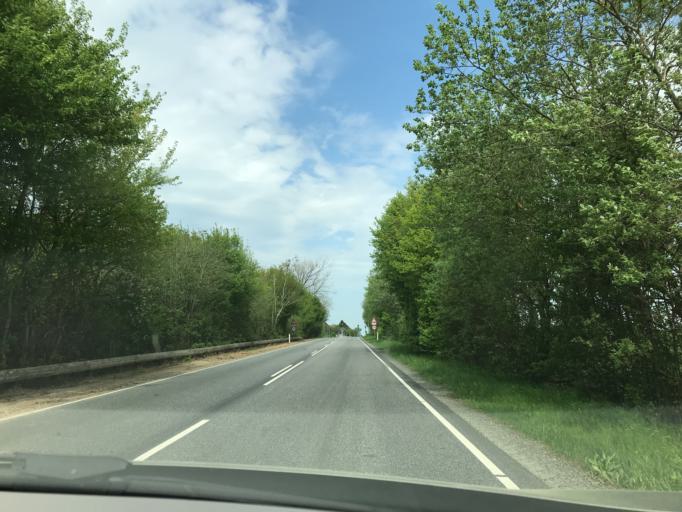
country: DK
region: South Denmark
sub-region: Assens Kommune
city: Assens
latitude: 55.2791
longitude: 9.9206
